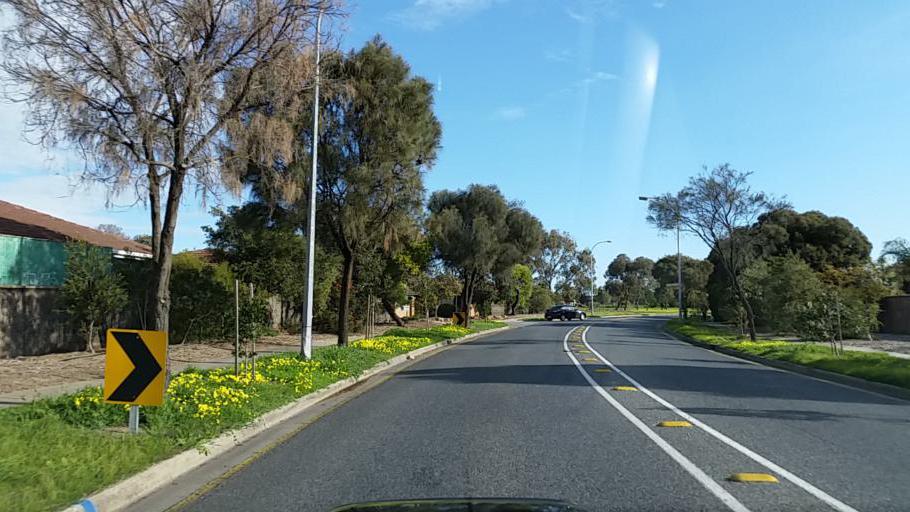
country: AU
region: South Australia
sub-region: Charles Sturt
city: West Lakes Shore
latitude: -34.8582
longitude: 138.4937
